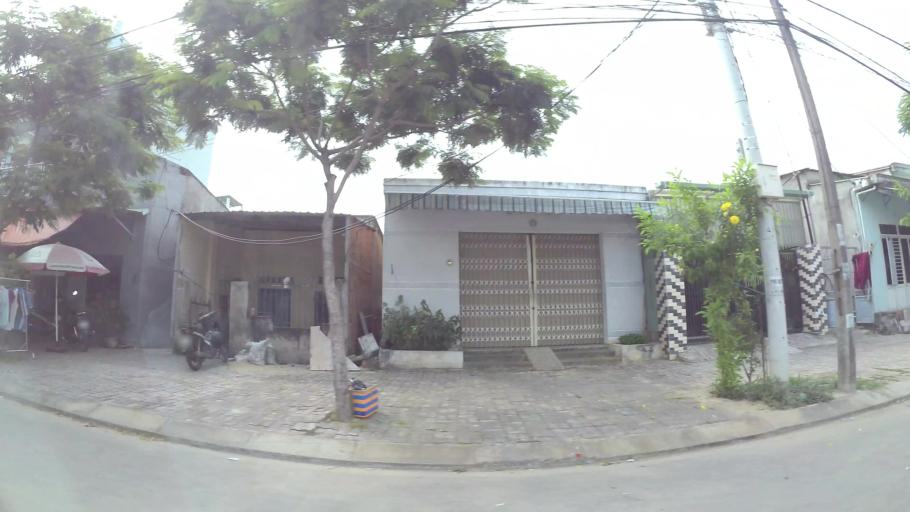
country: VN
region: Da Nang
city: Son Tra
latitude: 16.0867
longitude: 108.2432
